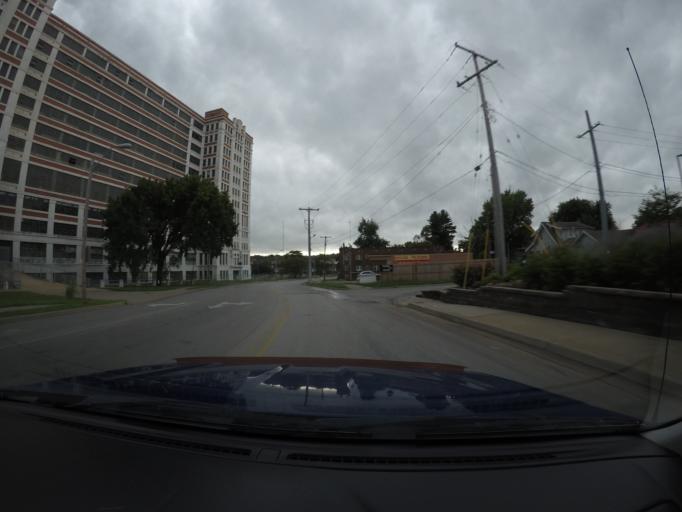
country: US
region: Missouri
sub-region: Clay County
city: North Kansas City
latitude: 39.1052
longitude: -94.5189
